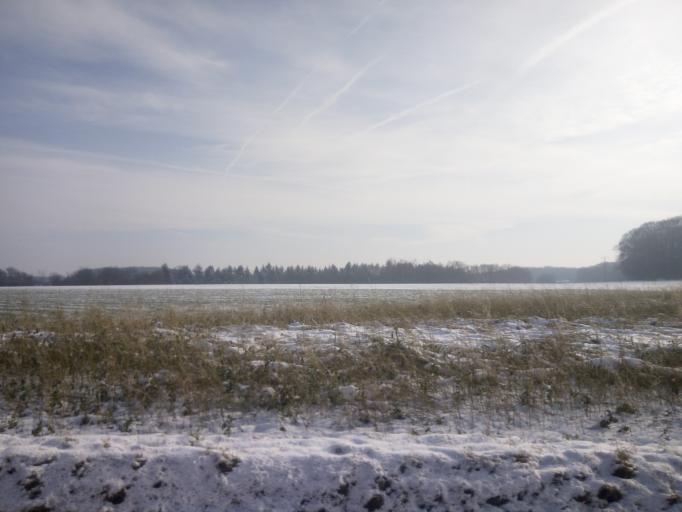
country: LU
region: Grevenmacher
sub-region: Canton d'Echternach
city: Consdorf
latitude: 49.7674
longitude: 6.3391
